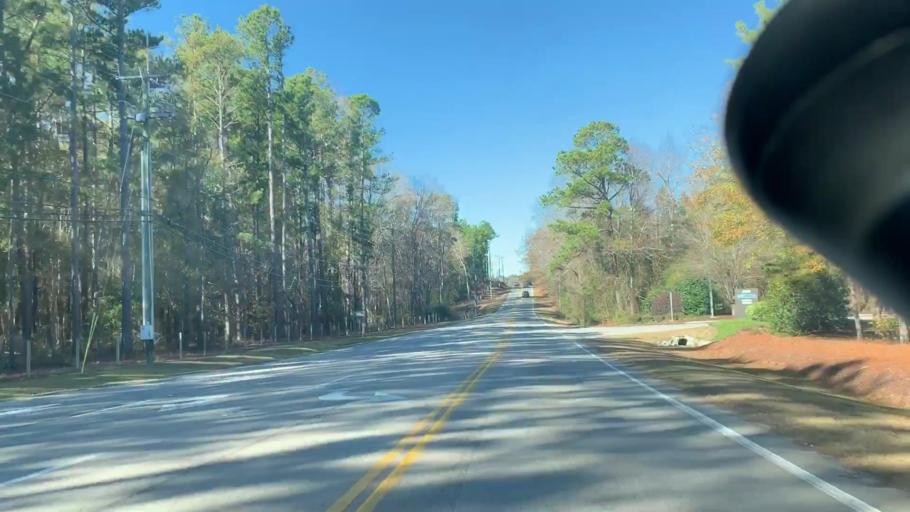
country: US
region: South Carolina
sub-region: Richland County
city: Woodfield
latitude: 34.0723
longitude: -80.9157
